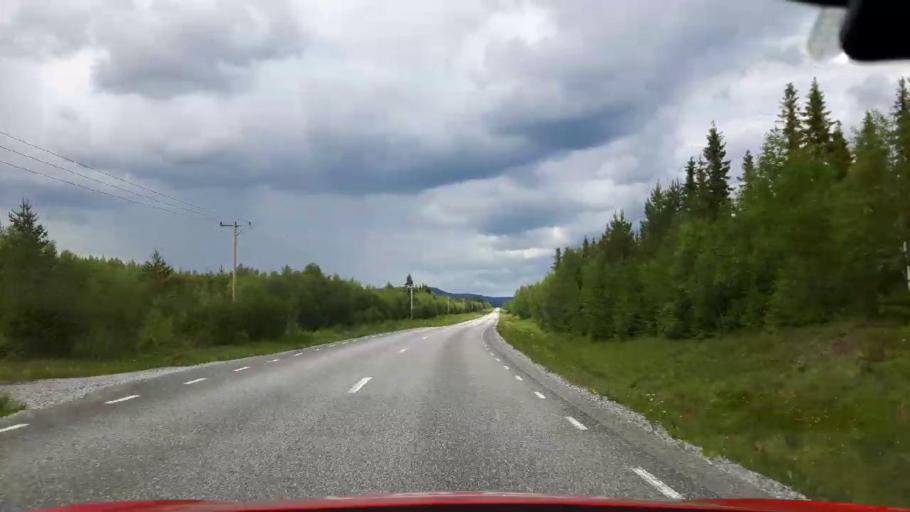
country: SE
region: Jaemtland
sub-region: Krokoms Kommun
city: Krokom
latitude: 63.6535
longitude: 14.3710
